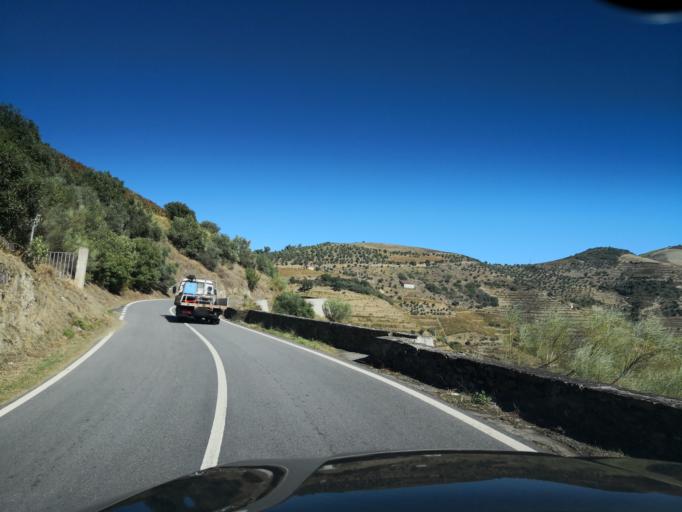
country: PT
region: Viseu
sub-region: Tabuaco
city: Tabuaco
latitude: 41.1684
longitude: -7.5137
